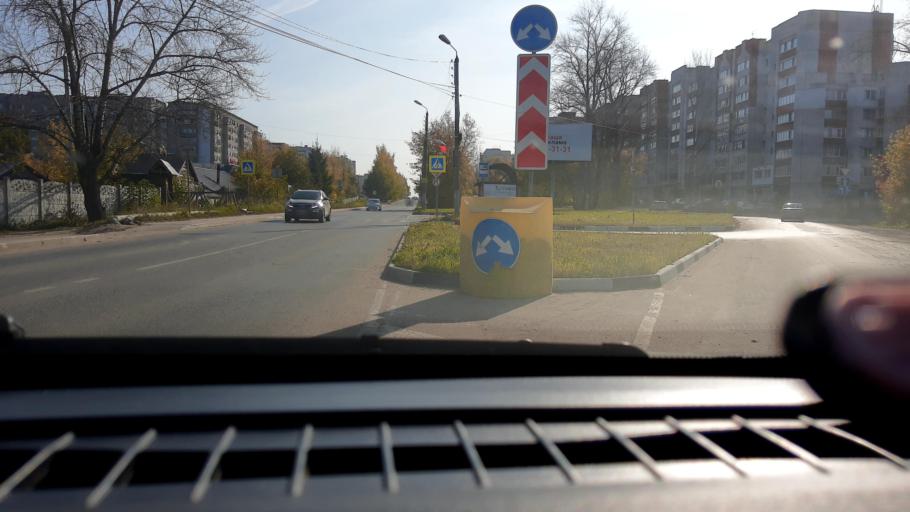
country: RU
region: Nizjnij Novgorod
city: Kstovo
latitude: 56.1597
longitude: 44.2068
